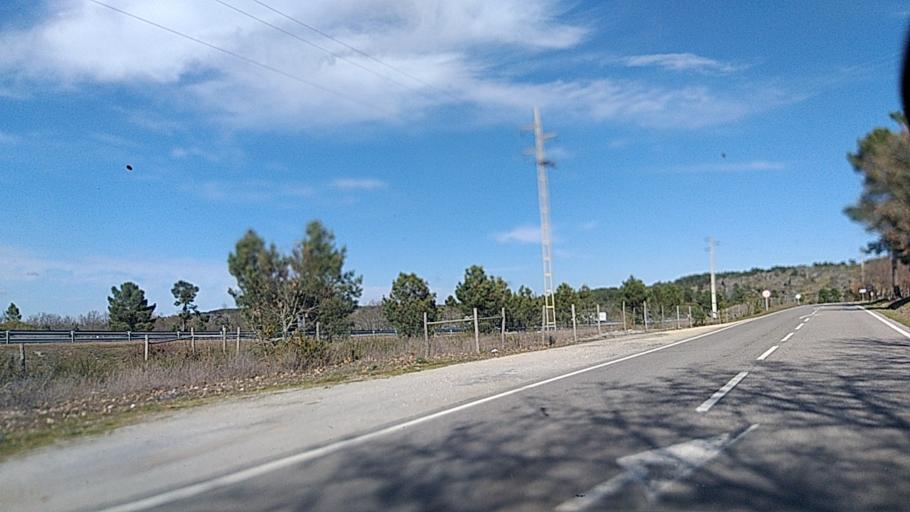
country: PT
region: Guarda
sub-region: Guarda
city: Sequeira
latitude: 40.5747
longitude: -7.1927
